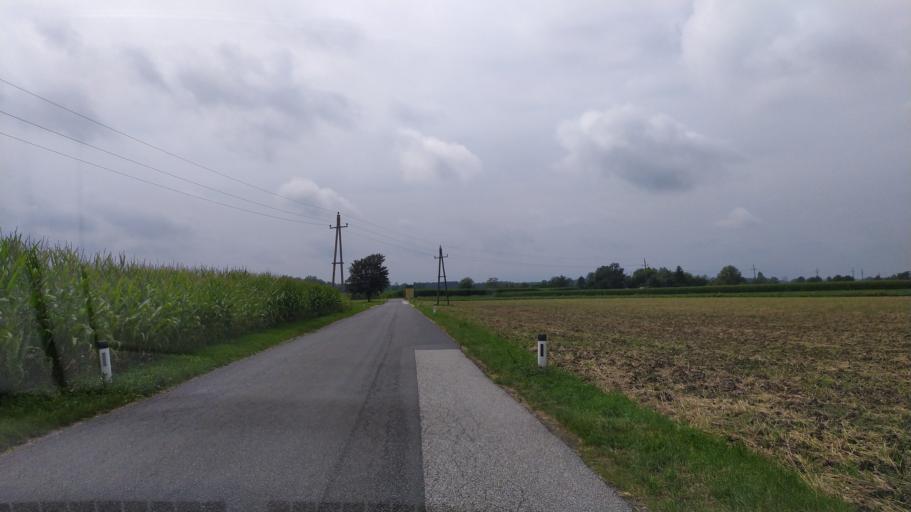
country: AT
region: Upper Austria
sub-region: Politischer Bezirk Perg
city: Bad Kreuzen
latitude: 48.1969
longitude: 14.7773
